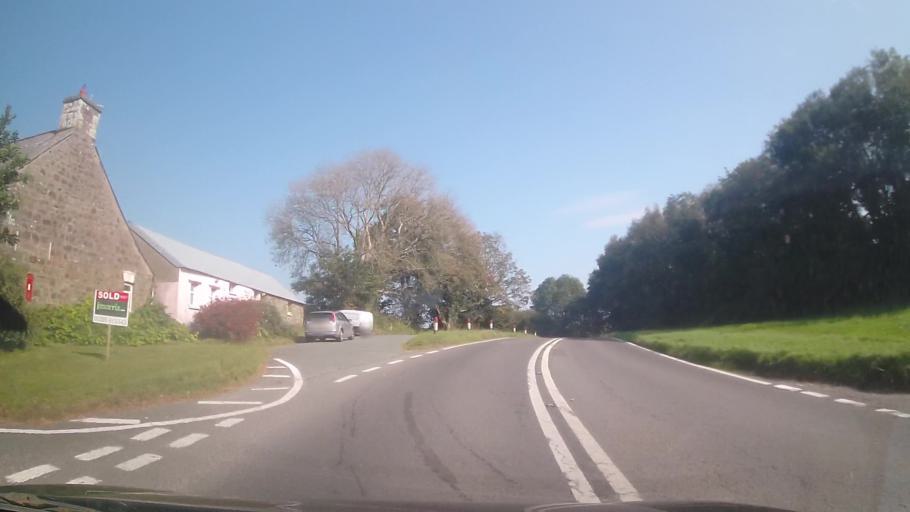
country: GB
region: Wales
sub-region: Pembrokeshire
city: Nevern
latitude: 52.0174
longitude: -4.7937
